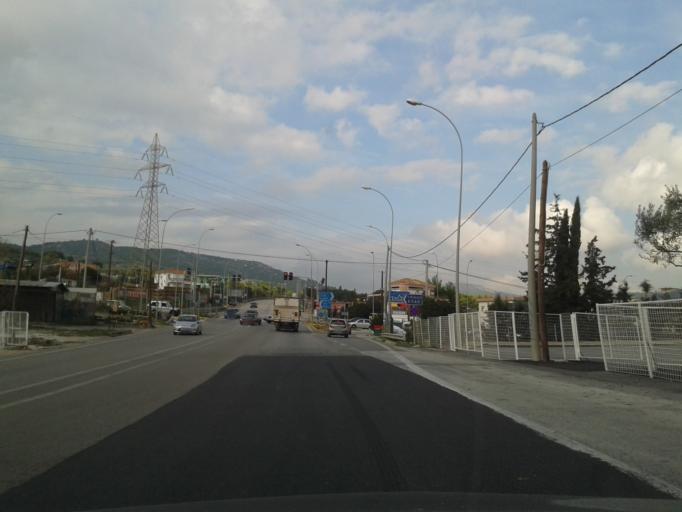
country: GR
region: Attica
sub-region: Nomarchia Anatolikis Attikis
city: Polydendri
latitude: 38.2020
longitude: 23.8574
